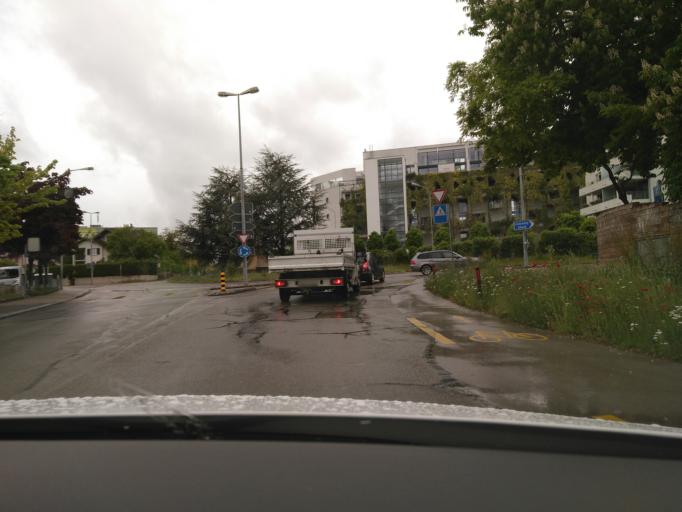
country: CH
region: Vaud
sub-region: Nyon District
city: Nyon
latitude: 46.3817
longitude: 6.2291
